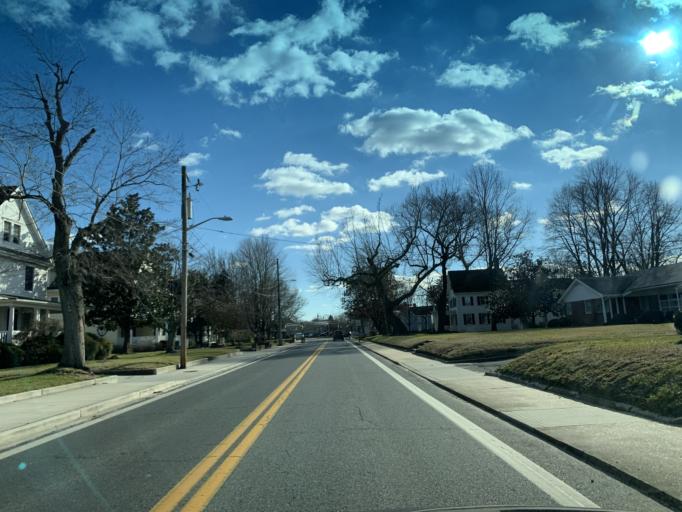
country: US
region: Maryland
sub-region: Worcester County
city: Berlin
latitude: 38.3281
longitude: -75.2204
